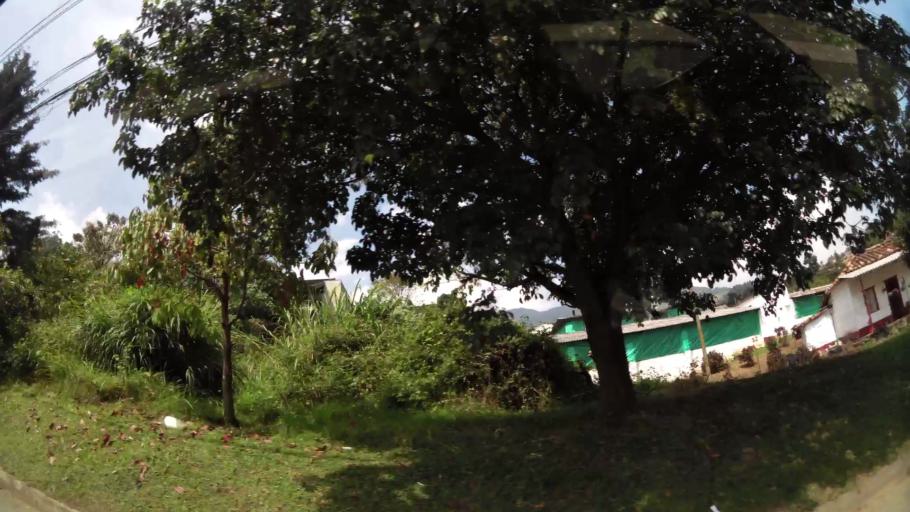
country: CO
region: Antioquia
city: La Estrella
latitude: 6.1777
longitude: -75.6539
